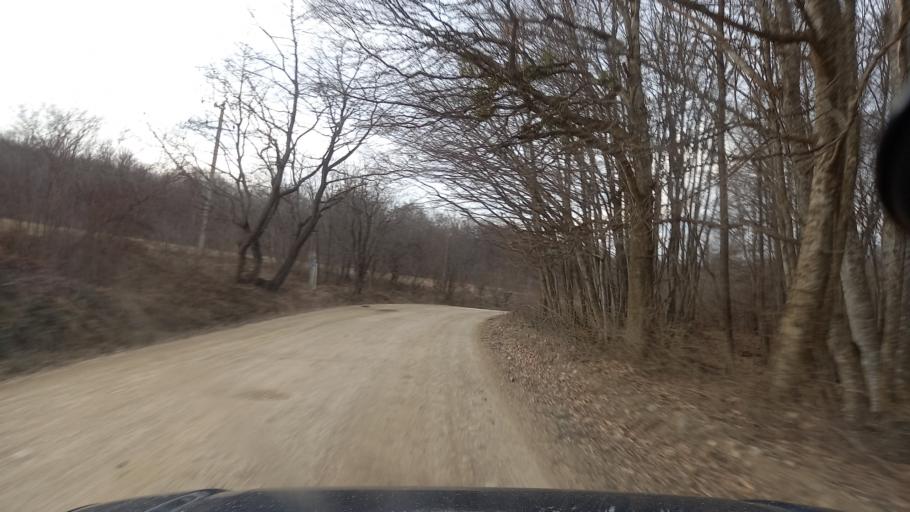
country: RU
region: Adygeya
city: Kamennomostskiy
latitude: 44.1473
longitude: 40.2492
